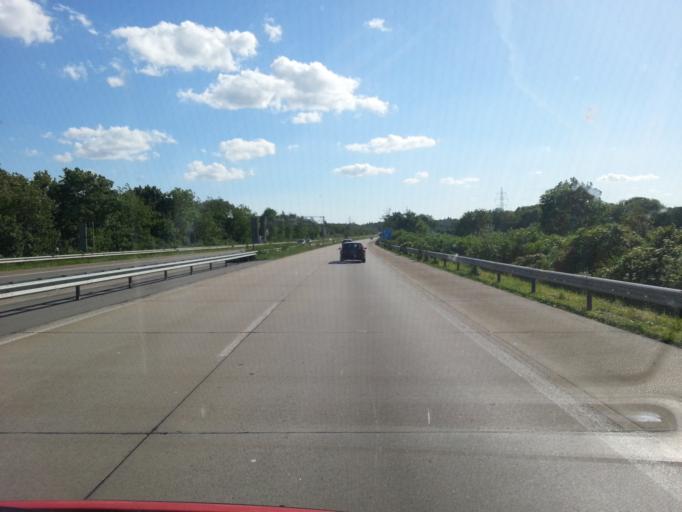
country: DE
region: Schleswig-Holstein
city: Sierksdorf
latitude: 54.0639
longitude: 10.7501
